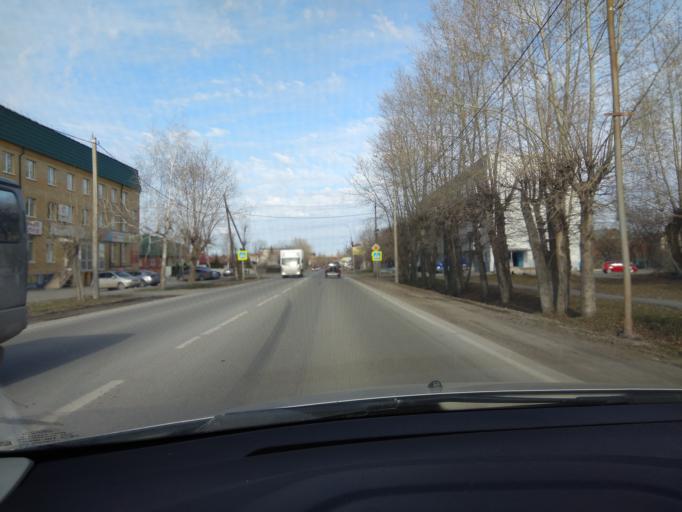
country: RU
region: Tjumen
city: Moskovskiy
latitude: 57.1563
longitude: 65.4466
